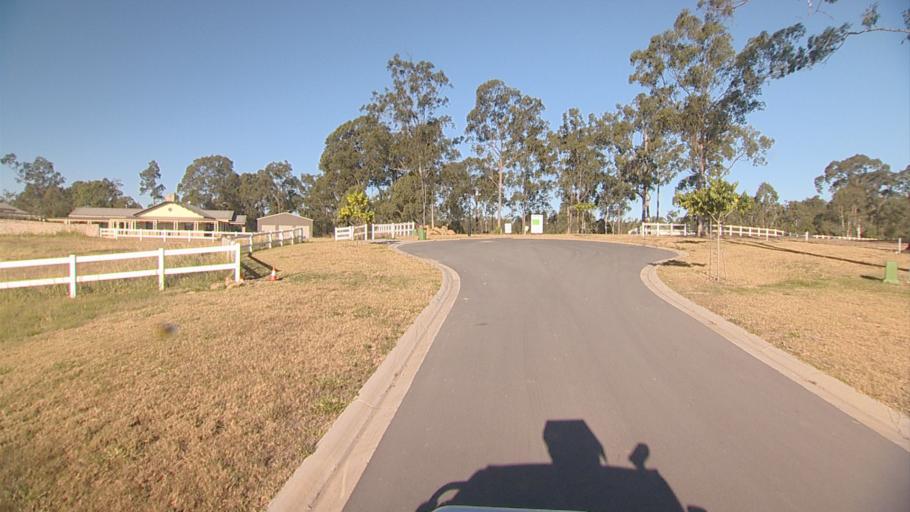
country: AU
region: Queensland
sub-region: Logan
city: North Maclean
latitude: -27.7936
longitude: 153.0235
